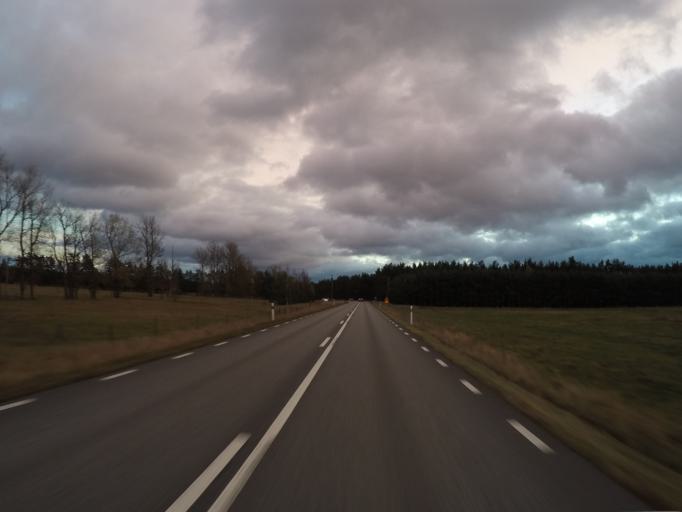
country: SE
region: Skane
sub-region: Kristianstads Kommun
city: Degeberga
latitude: 55.8812
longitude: 14.0870
